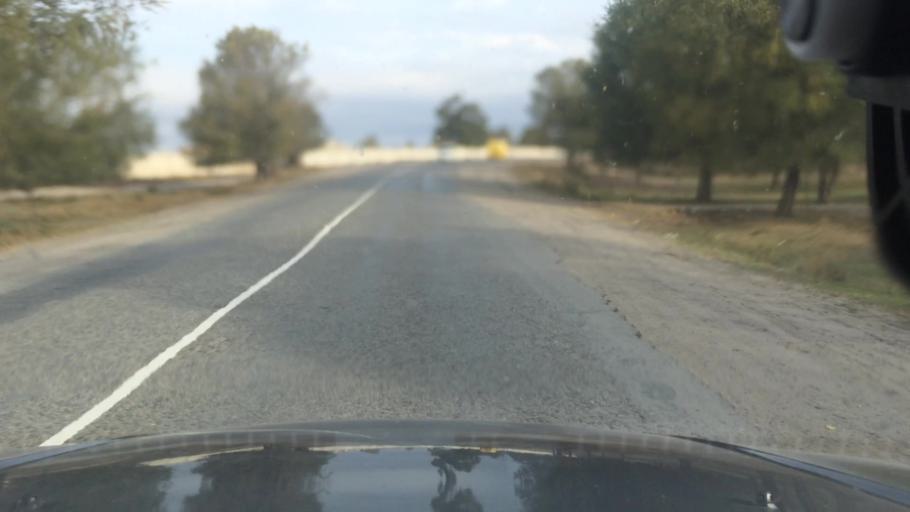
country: KG
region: Ysyk-Koel
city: Karakol
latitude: 42.5360
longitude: 78.3819
